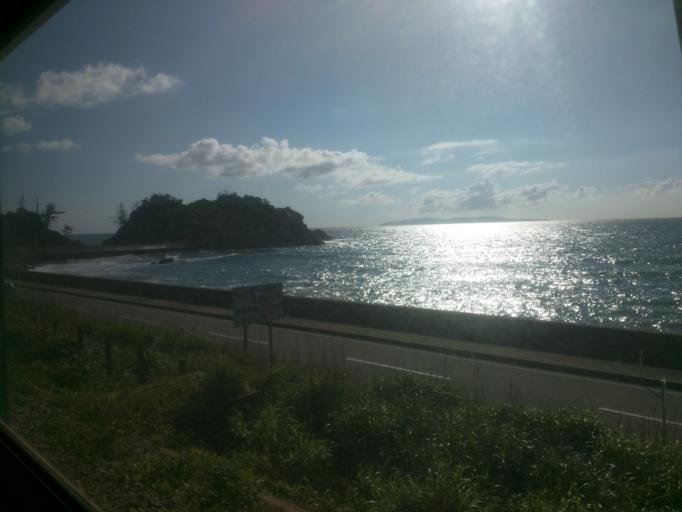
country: JP
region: Niigata
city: Murakami
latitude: 38.4460
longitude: 139.4871
